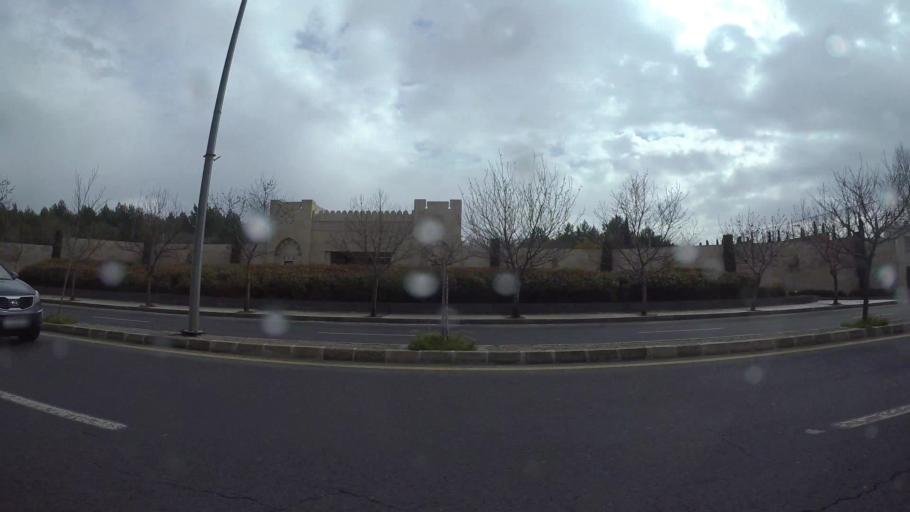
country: JO
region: Amman
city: Wadi as Sir
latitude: 31.9816
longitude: 35.8217
